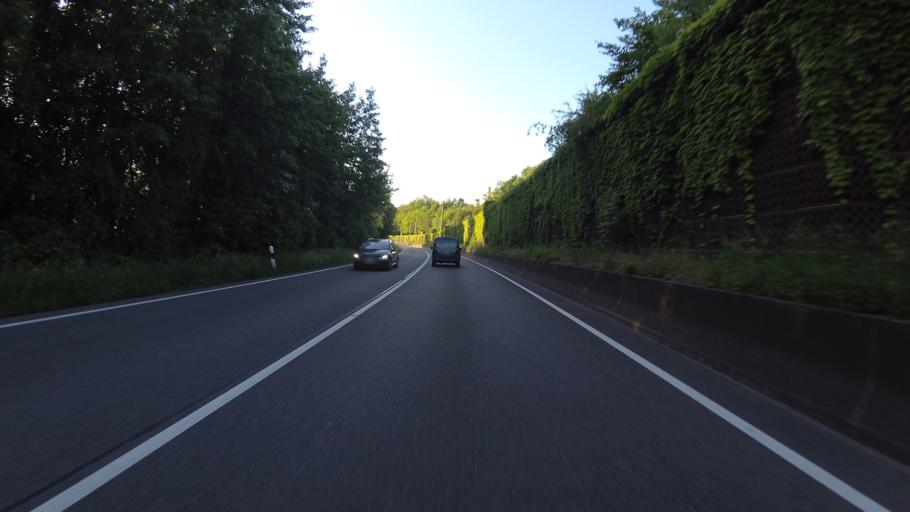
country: DE
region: Saarland
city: Kleinblittersdorf
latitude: 49.1625
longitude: 7.0341
